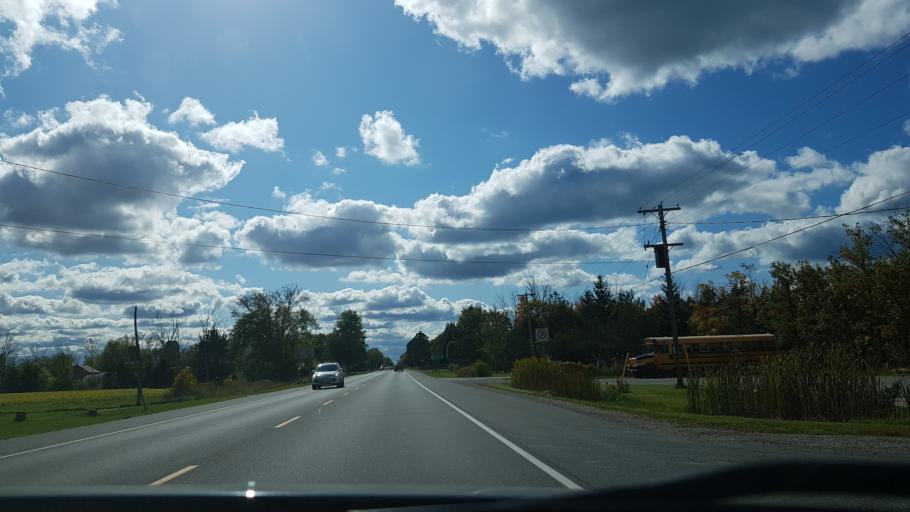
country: CA
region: Ontario
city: Bluewater
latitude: 43.3326
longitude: -81.7402
